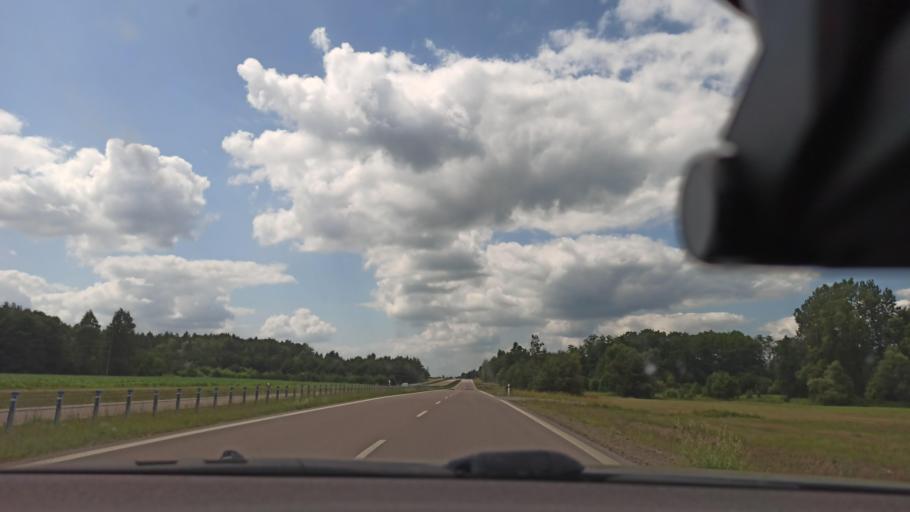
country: PL
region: Podlasie
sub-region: Powiat bialostocki
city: Turosn Koscielna
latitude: 53.0168
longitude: 22.9980
